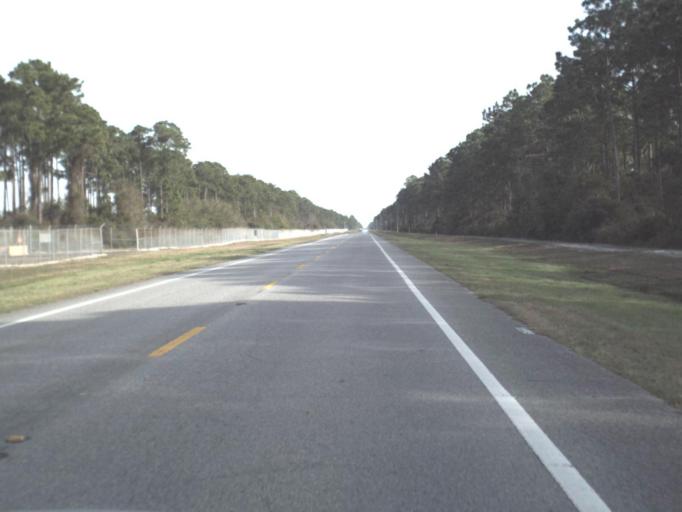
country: US
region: Florida
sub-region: Bay County
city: Tyndall Air Force Base
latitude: 30.0581
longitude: -85.5749
